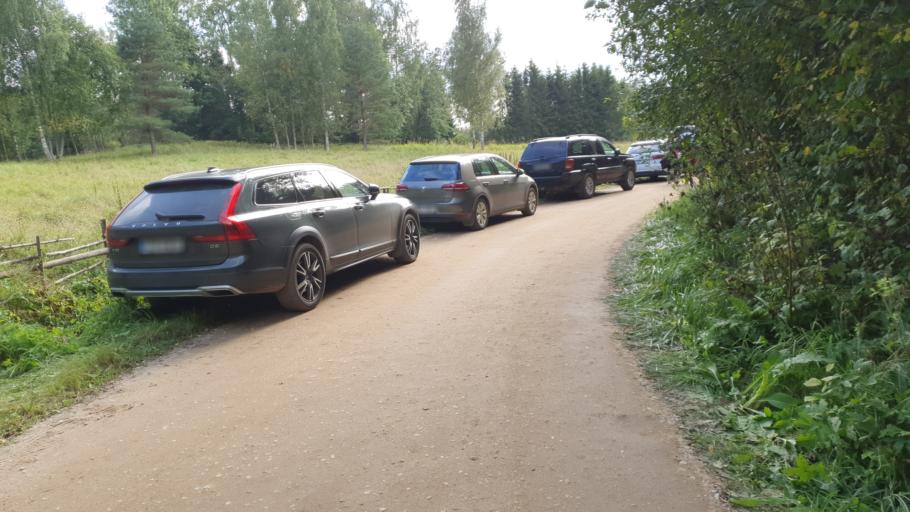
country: EE
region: Tartu
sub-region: UElenurme vald
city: Ulenurme
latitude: 58.1315
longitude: 26.7491
